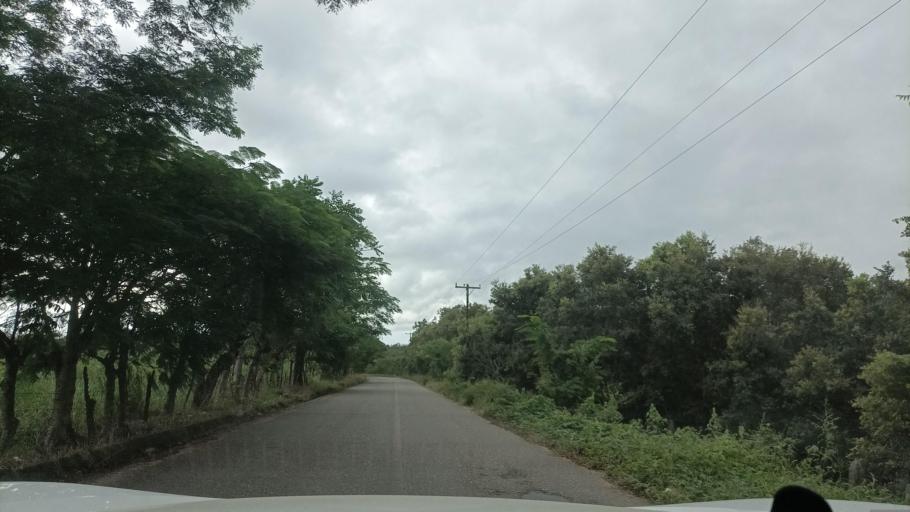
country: MX
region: Veracruz
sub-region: Cosoleacaque
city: Coacotla
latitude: 17.9463
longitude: -94.7175
